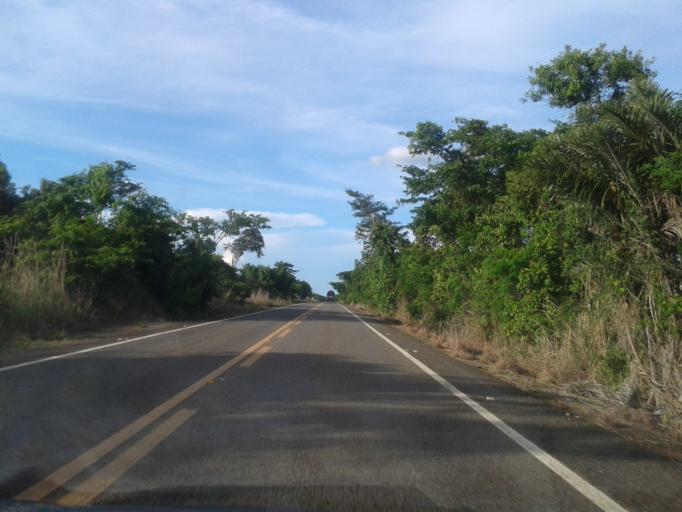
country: BR
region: Goias
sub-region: Sao Miguel Do Araguaia
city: Sao Miguel do Araguaia
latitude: -13.7052
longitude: -50.3326
